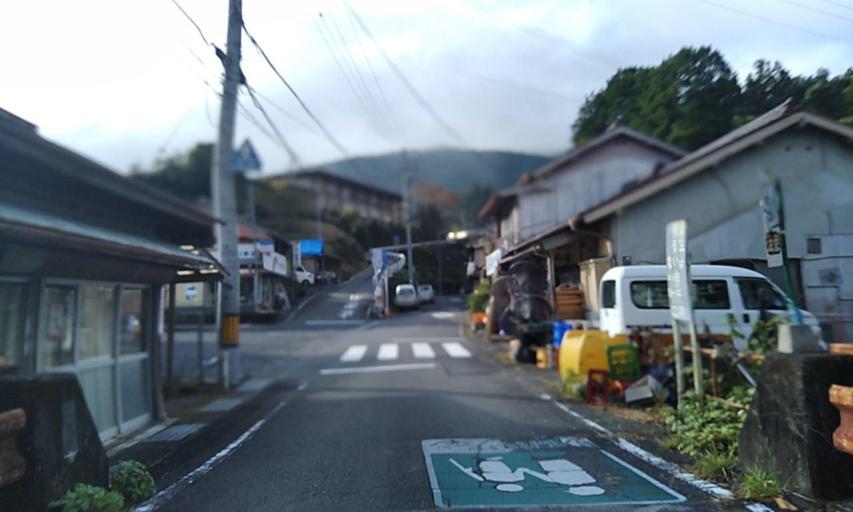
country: JP
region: Wakayama
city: Shingu
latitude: 33.9229
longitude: 135.9831
